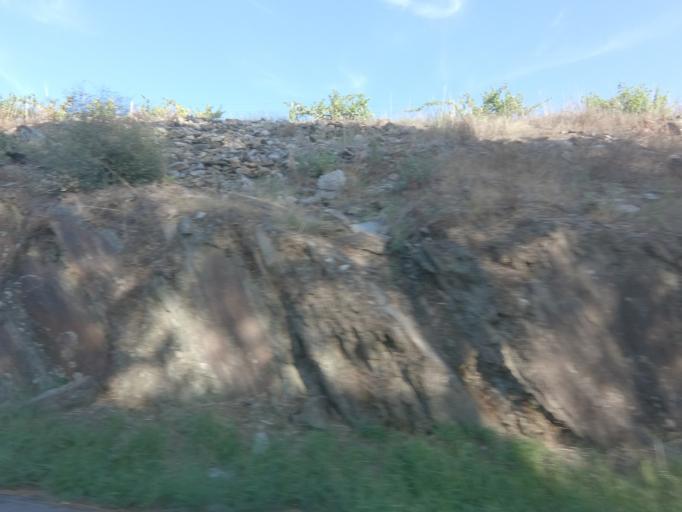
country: PT
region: Vila Real
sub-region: Sabrosa
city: Sabrosa
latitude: 41.2471
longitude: -7.5239
